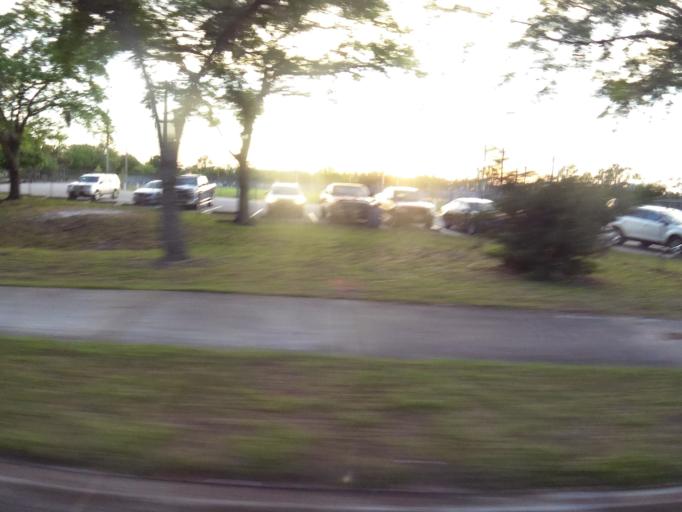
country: US
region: Florida
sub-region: Duval County
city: Jacksonville
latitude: 30.2708
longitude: -81.5916
